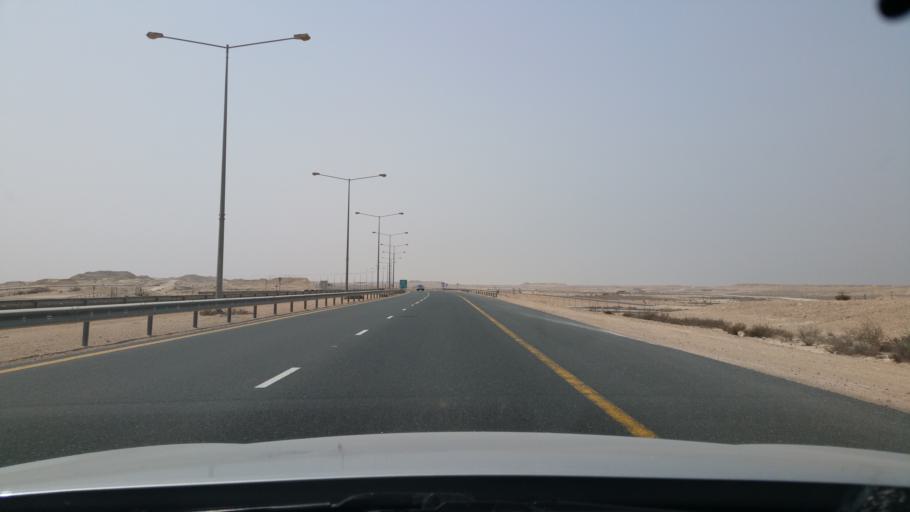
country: QA
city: Umm Bab
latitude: 25.2706
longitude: 50.7928
